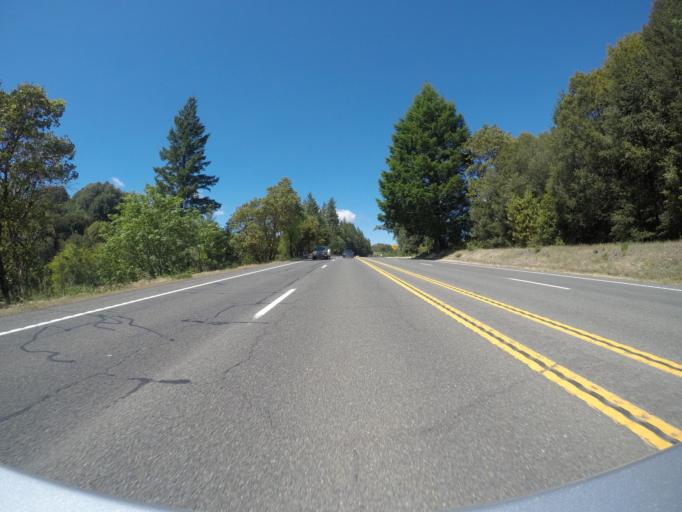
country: US
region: California
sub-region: Mendocino County
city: Laytonville
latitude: 39.6216
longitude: -123.4651
